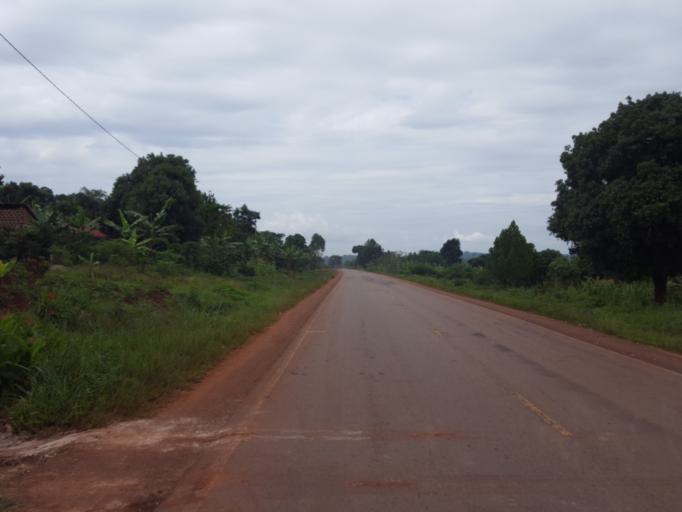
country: UG
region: Central Region
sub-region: Mityana District
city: Mityana
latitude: 0.6473
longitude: 32.0961
